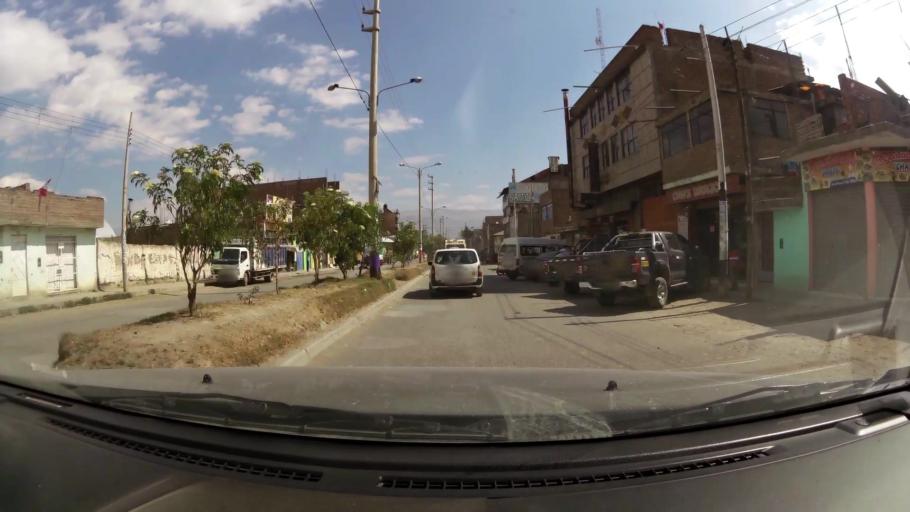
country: PE
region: Junin
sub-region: Provincia de Huancayo
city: Huancayo
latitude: -12.0863
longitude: -75.2000
